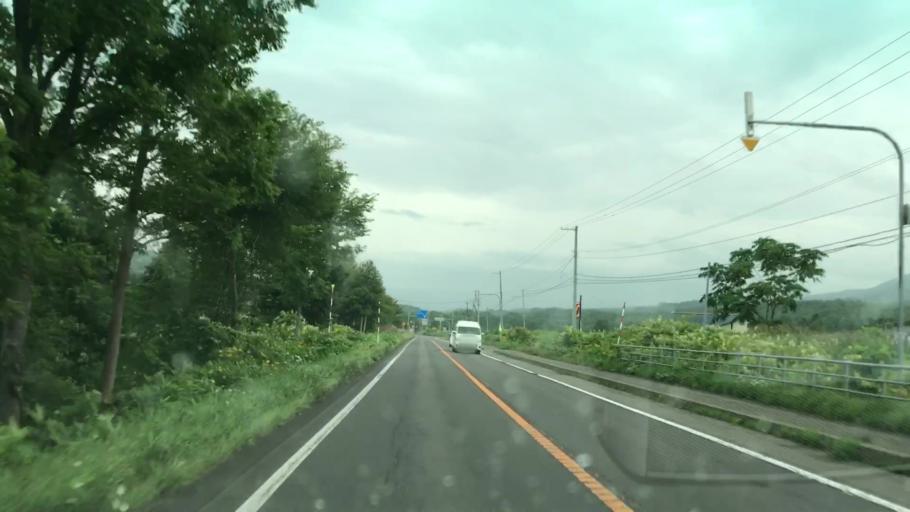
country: JP
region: Hokkaido
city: Niseko Town
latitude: 42.7675
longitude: 140.4846
